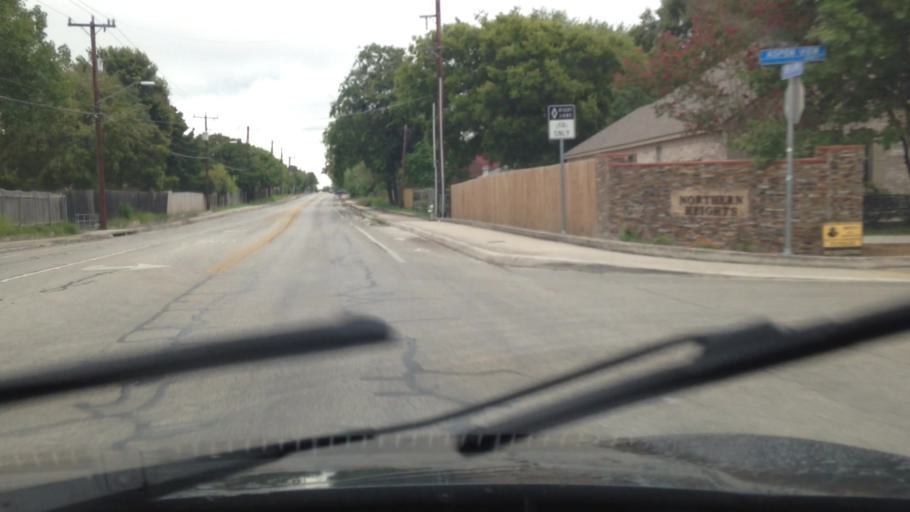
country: US
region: Texas
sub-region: Bexar County
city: Windcrest
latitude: 29.5622
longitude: -98.3997
